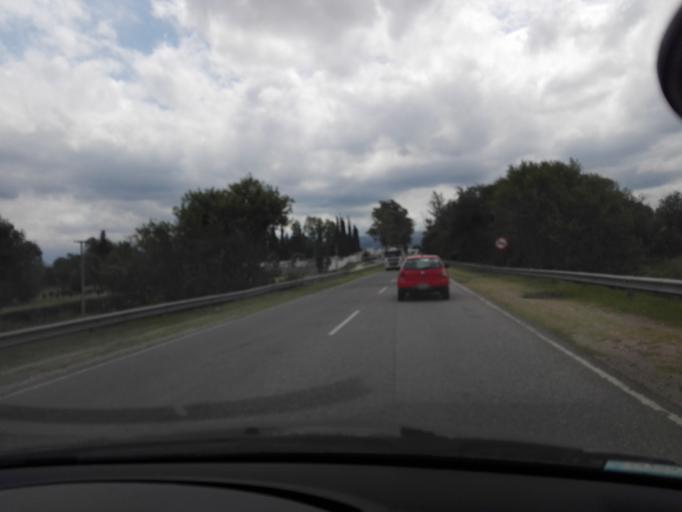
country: AR
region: Cordoba
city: Alta Gracia
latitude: -31.6584
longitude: -64.4036
